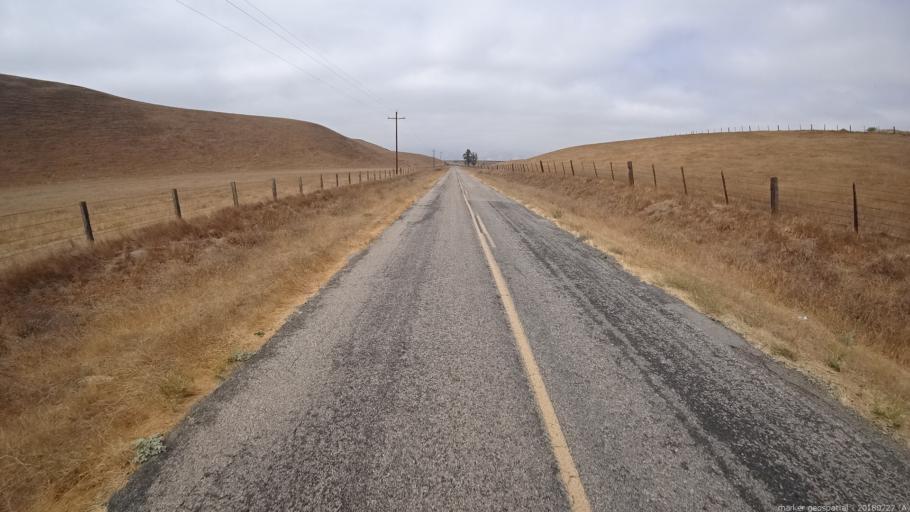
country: US
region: California
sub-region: Monterey County
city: King City
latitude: 36.2230
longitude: -121.0695
